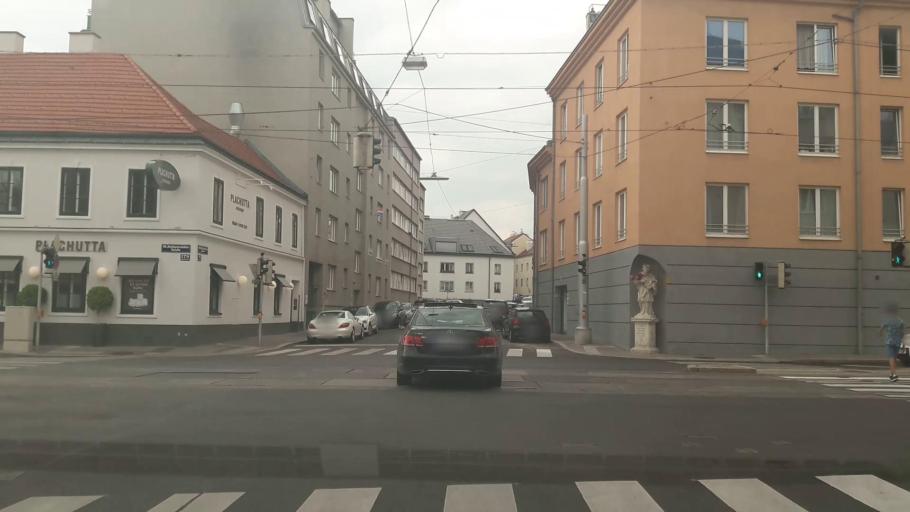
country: AT
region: Lower Austria
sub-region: Politischer Bezirk Korneuburg
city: Langenzersdorf
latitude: 48.2580
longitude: 16.3672
